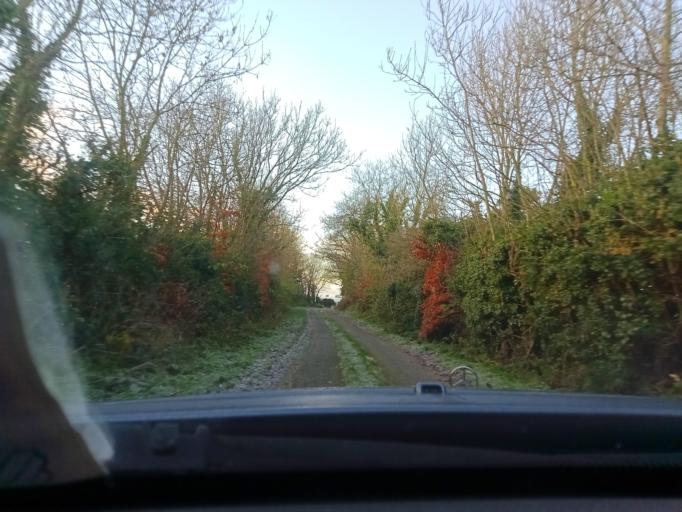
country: IE
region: Leinster
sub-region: County Carlow
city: Bagenalstown
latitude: 52.6474
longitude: -6.9974
